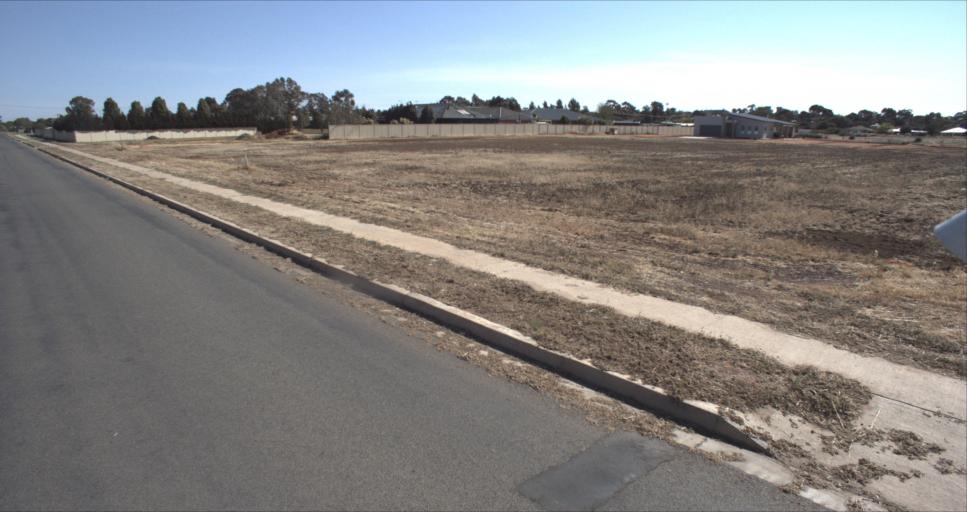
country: AU
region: New South Wales
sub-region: Leeton
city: Leeton
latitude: -34.5484
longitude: 146.4177
